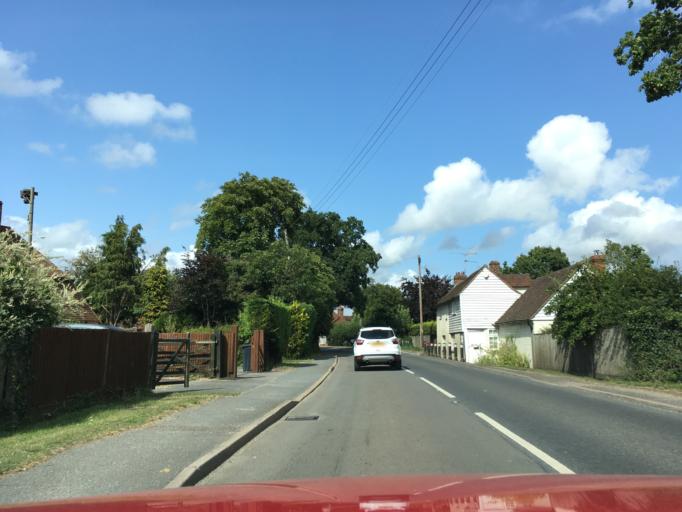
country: GB
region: England
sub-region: Kent
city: Headcorn
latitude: 51.1236
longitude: 0.6481
